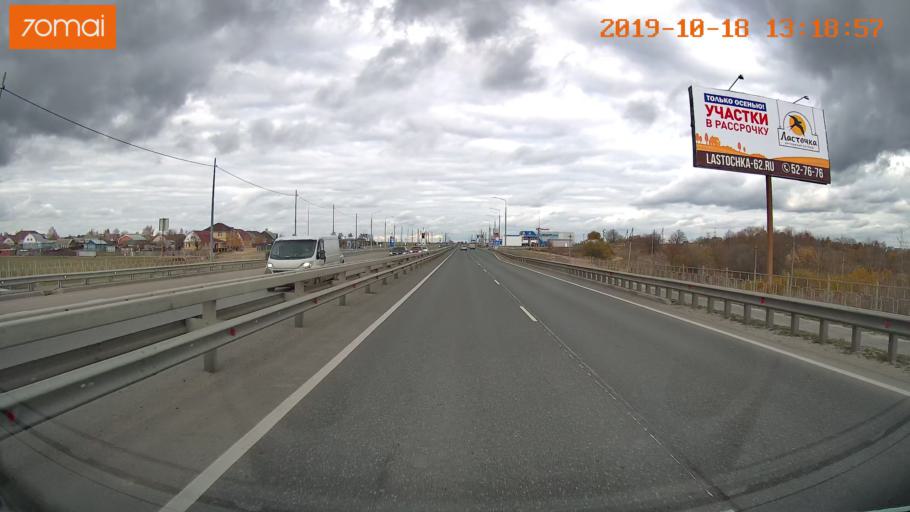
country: RU
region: Rjazan
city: Polyany
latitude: 54.6614
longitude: 39.8217
